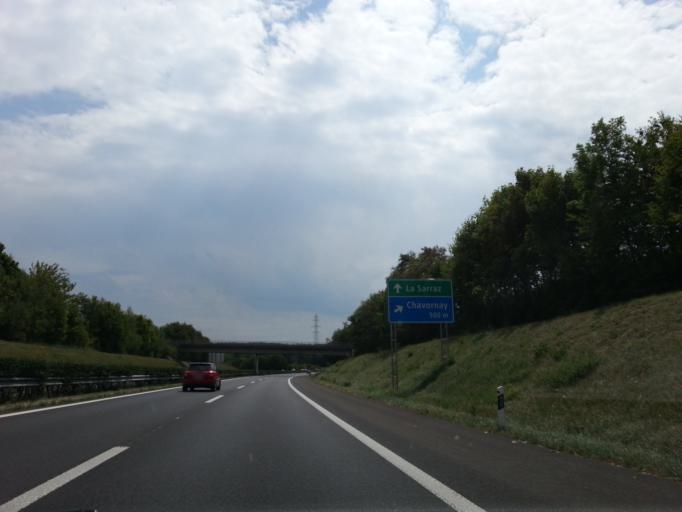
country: CH
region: Vaud
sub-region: Jura-Nord vaudois District
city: Chavornay
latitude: 46.7154
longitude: 6.5772
